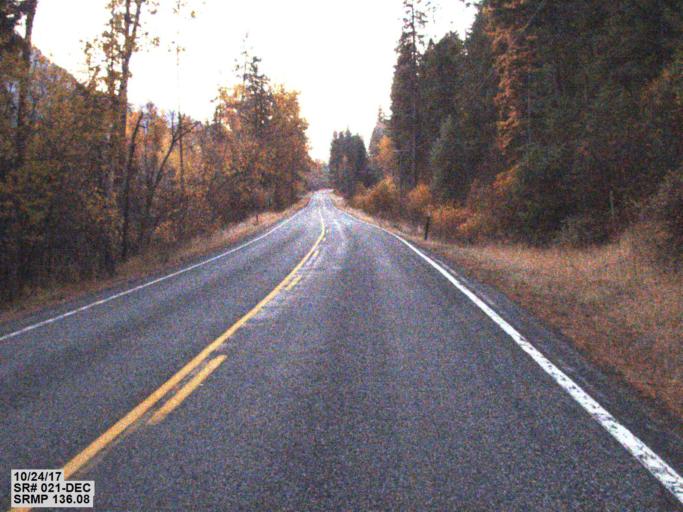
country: US
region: Washington
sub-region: Ferry County
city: Republic
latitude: 48.3356
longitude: -118.7487
